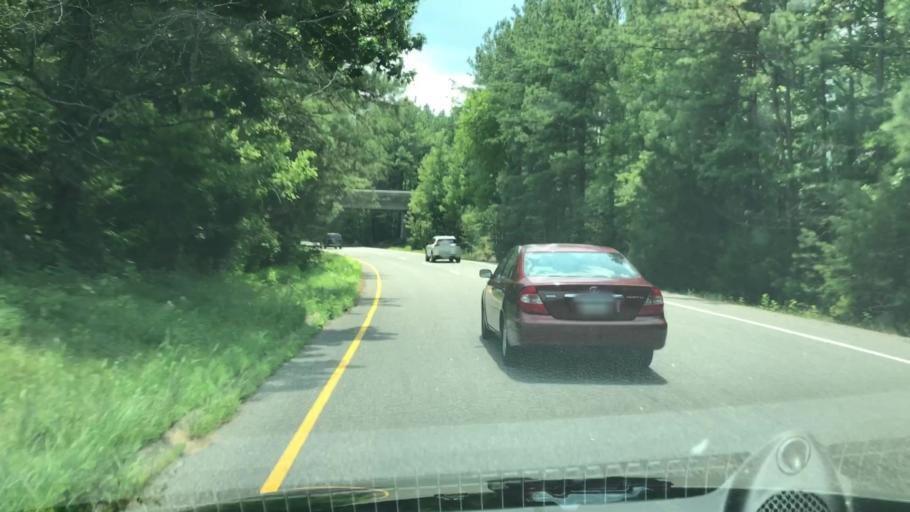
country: US
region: Virginia
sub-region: Hanover County
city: Ashland
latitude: 37.8458
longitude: -77.4552
